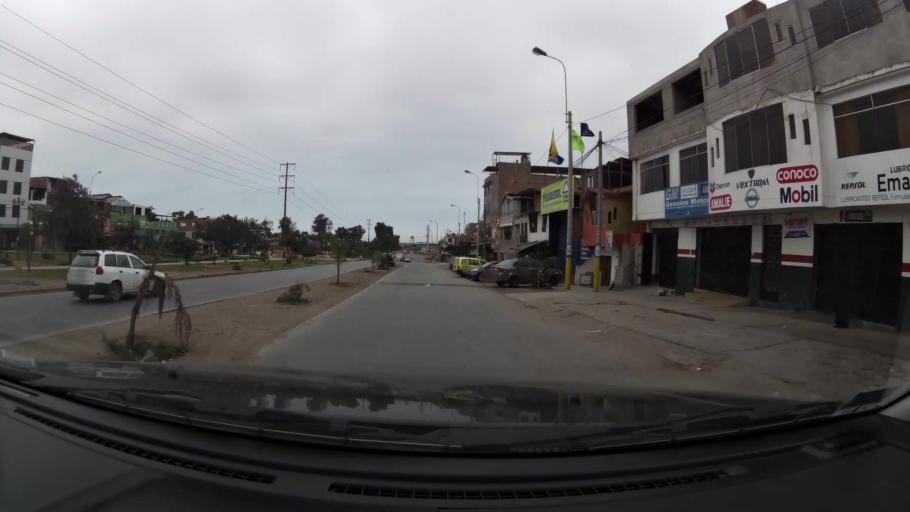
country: PE
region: Lima
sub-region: Lima
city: Surco
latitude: -12.1968
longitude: -76.9556
